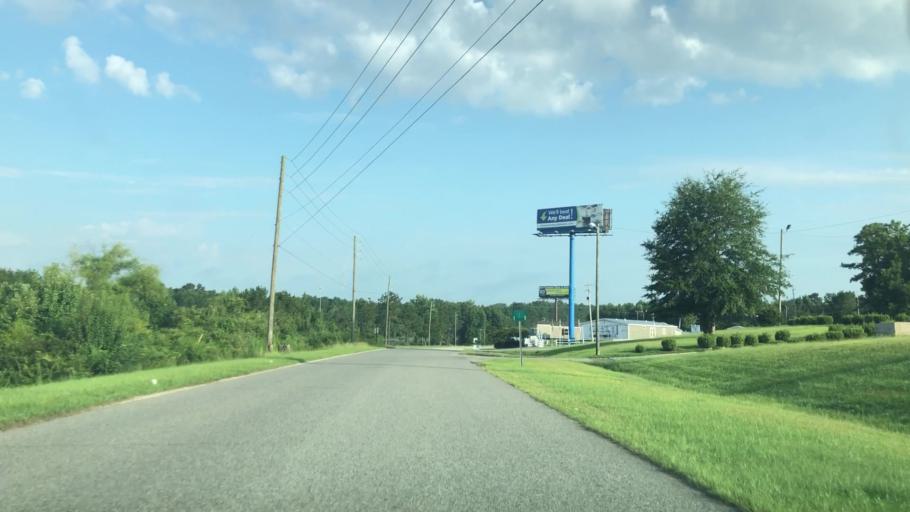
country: US
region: Alabama
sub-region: Chilton County
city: Clanton
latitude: 32.8034
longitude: -86.5784
